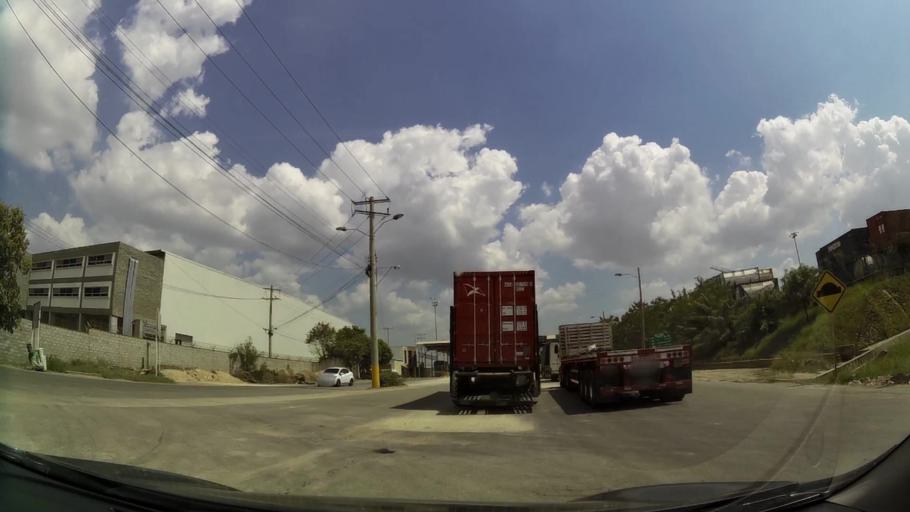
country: CO
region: Bolivar
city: Cartagena
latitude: 10.3424
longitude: -75.4917
